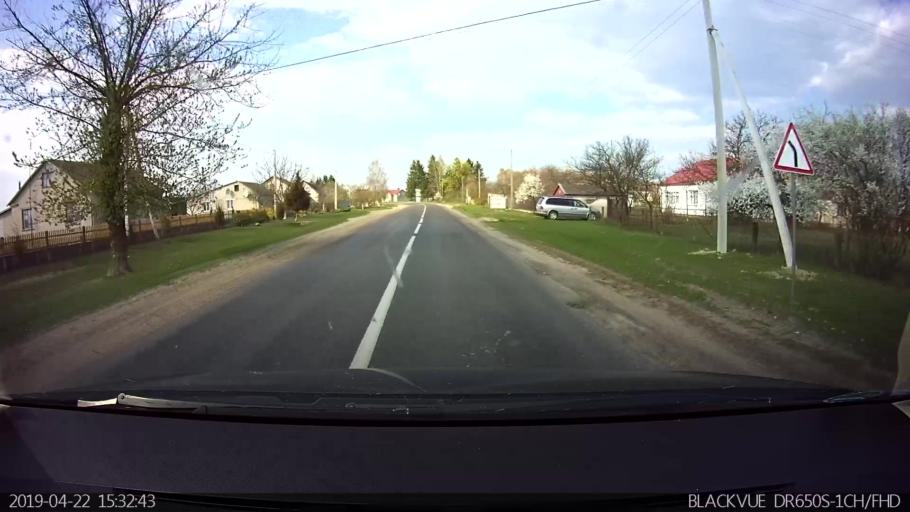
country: BY
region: Brest
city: Vysokaye
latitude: 52.4101
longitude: 23.3842
